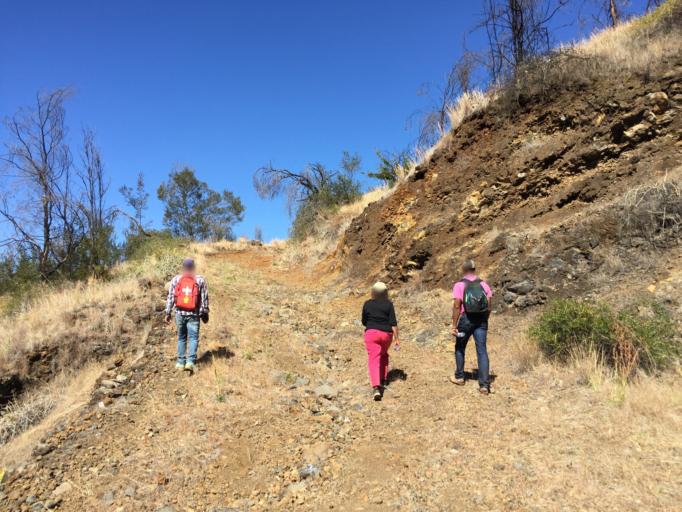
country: CV
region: Mosteiros
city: Porto dos Mosteiros
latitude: 15.0064
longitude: -24.3609
